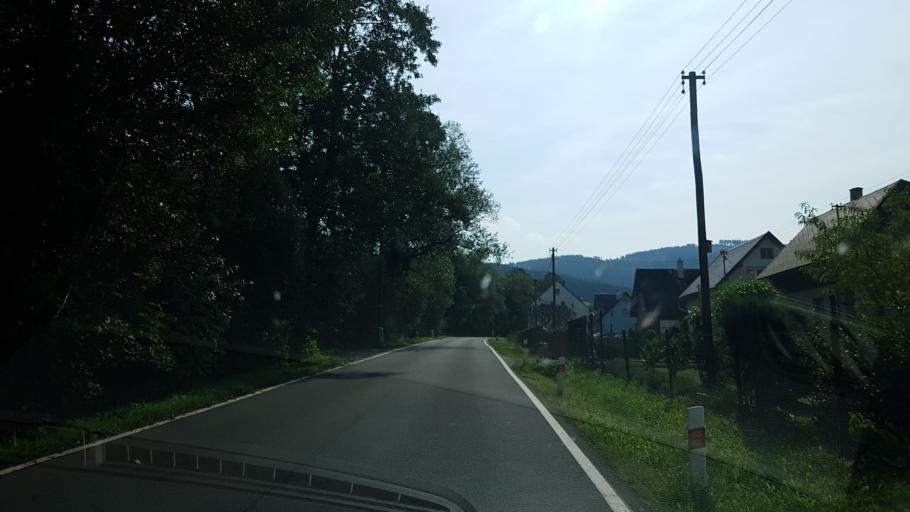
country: CZ
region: Olomoucky
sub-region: Okres Jesenik
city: Jesenik
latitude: 50.2153
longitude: 17.2198
